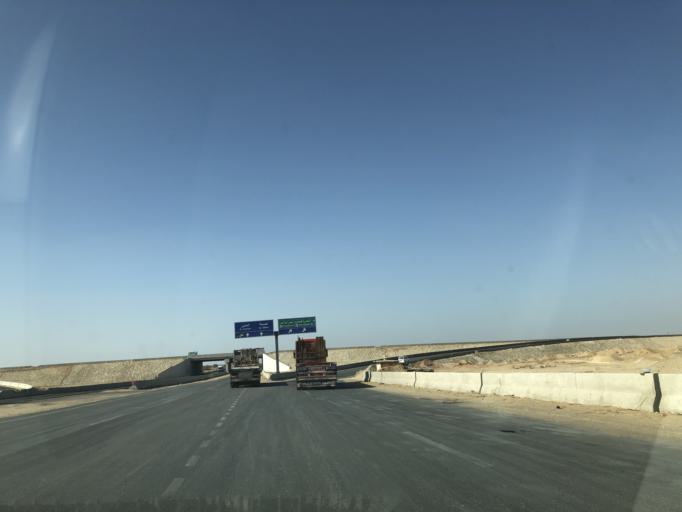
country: EG
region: Muhafazat al Minufiyah
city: Ashmun
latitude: 30.0649
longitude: 30.8459
